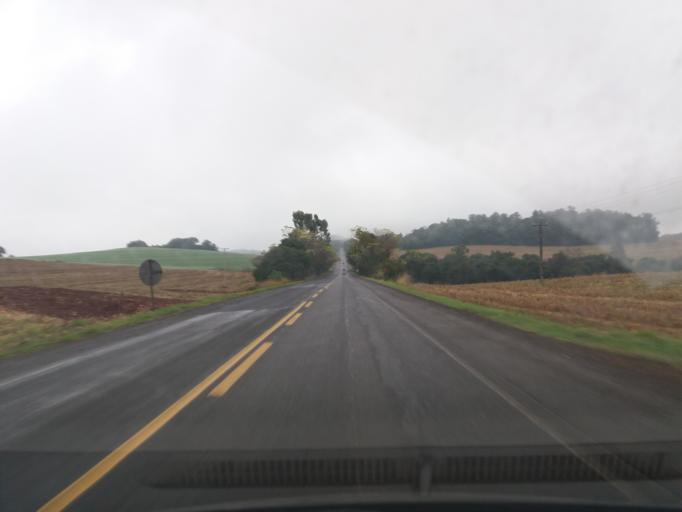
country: BR
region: Parana
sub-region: Ampere
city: Ampere
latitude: -25.8686
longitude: -53.4871
